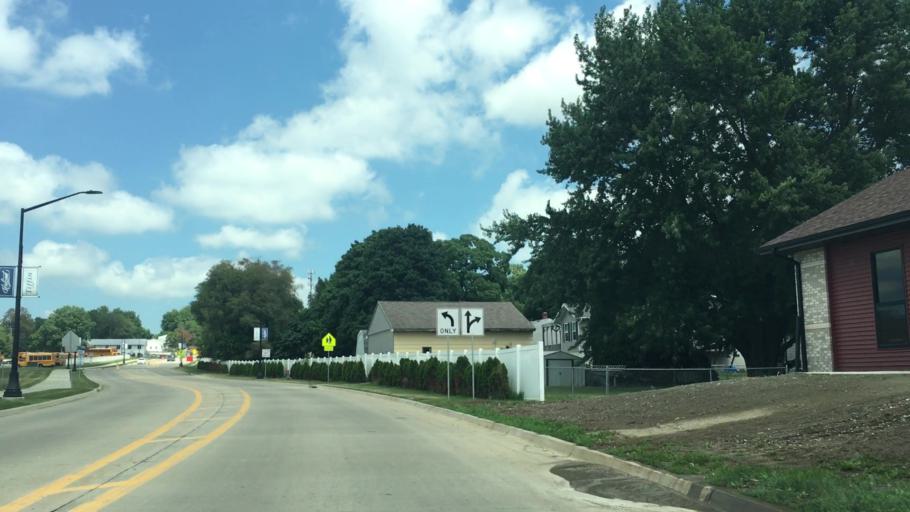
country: US
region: Iowa
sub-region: Johnson County
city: Tiffin
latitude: 41.7043
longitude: -91.6665
